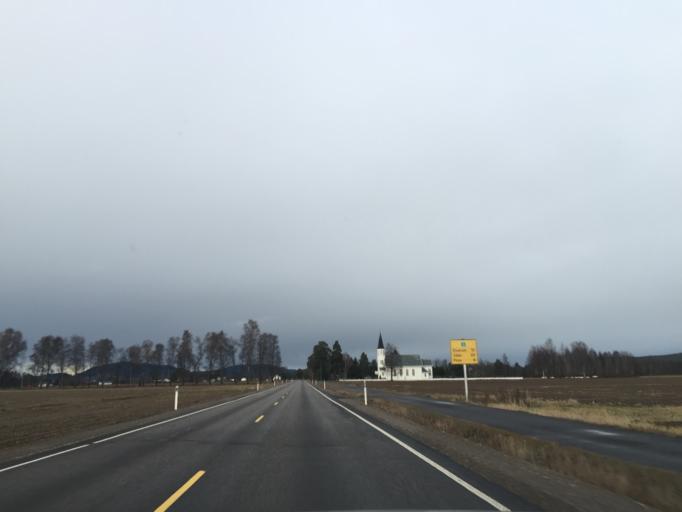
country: NO
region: Hedmark
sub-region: Asnes
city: Flisa
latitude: 60.5646
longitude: 12.0588
